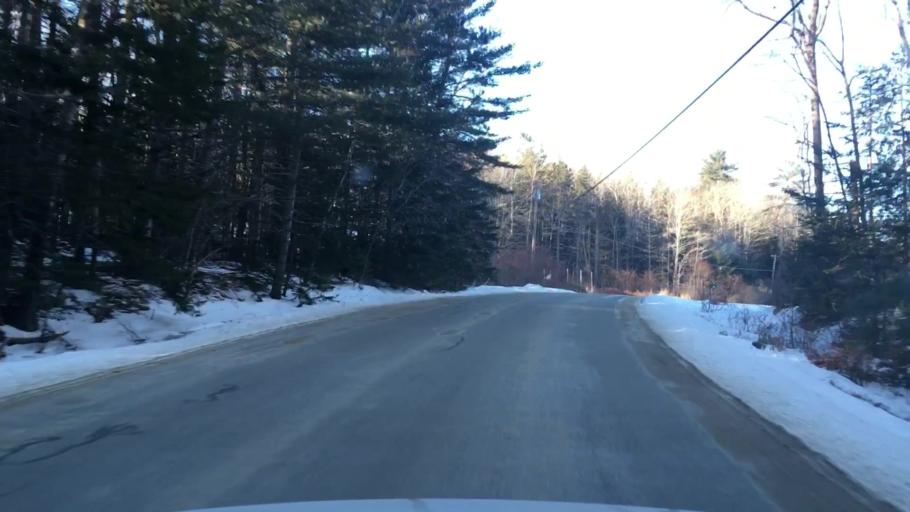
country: US
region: Maine
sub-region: Hancock County
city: Castine
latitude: 44.3409
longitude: -68.7831
